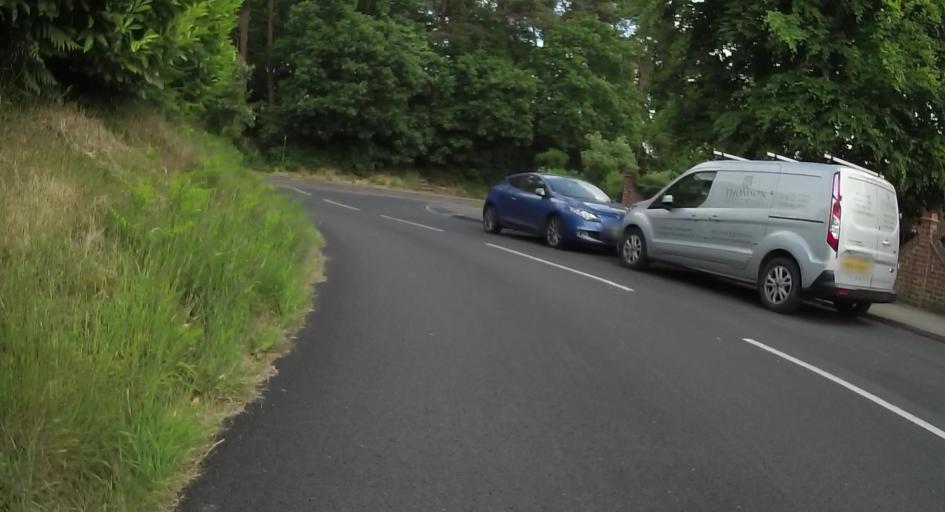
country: GB
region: England
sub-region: Surrey
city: Hale
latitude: 51.2374
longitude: -0.7852
